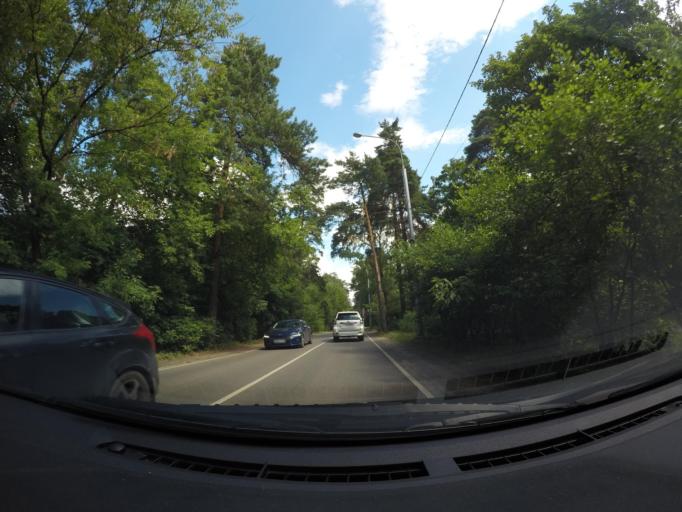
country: RU
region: Moskovskaya
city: Malakhovka
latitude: 55.6444
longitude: 38.0340
